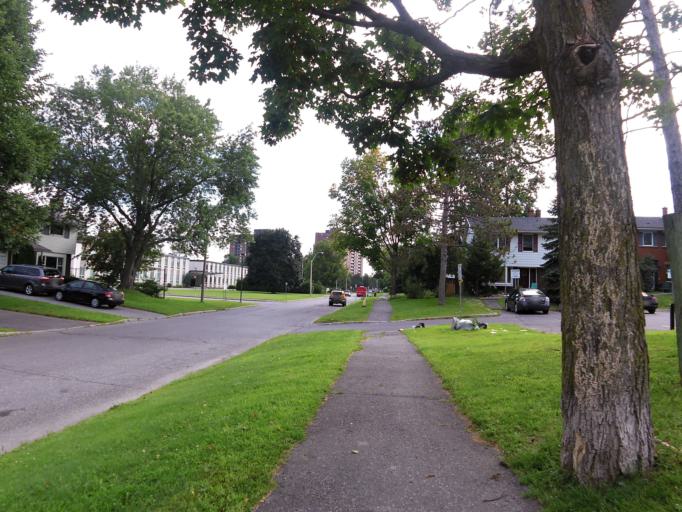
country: CA
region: Ontario
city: Bells Corners
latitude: 45.3403
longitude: -75.7937
